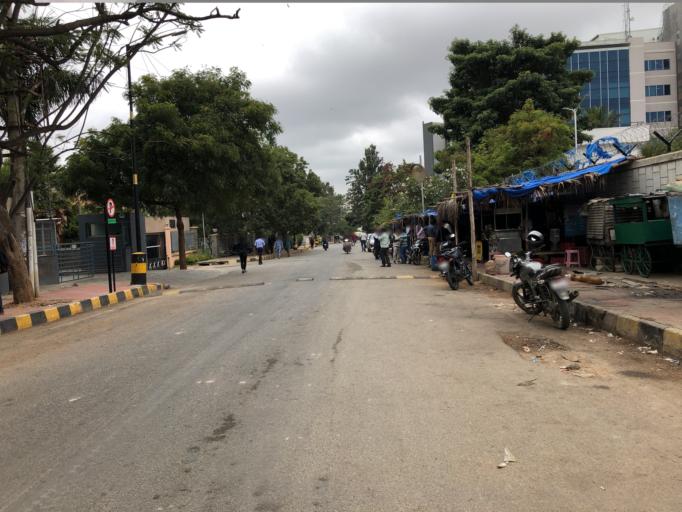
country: IN
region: Karnataka
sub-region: Bangalore Rural
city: Hoskote
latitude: 12.9847
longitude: 77.7284
